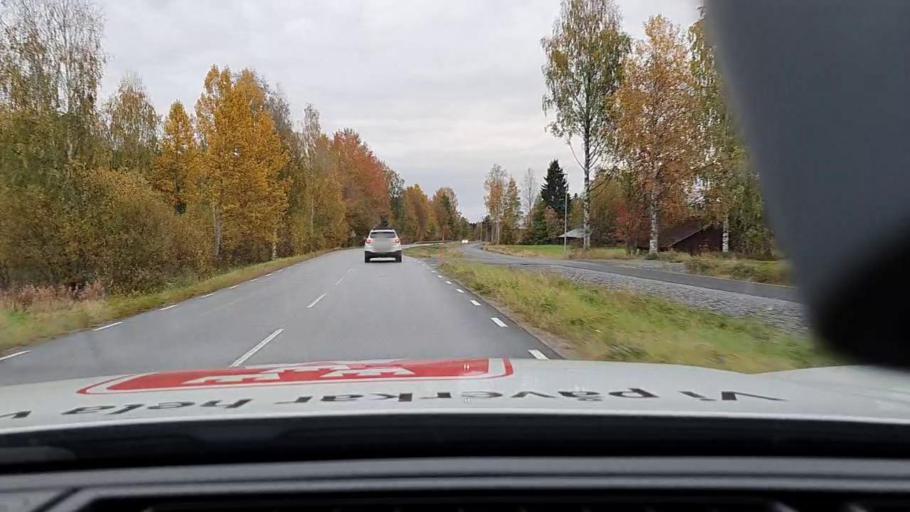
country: SE
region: Norrbotten
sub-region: Bodens Kommun
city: Saevast
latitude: 65.7708
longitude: 21.7032
